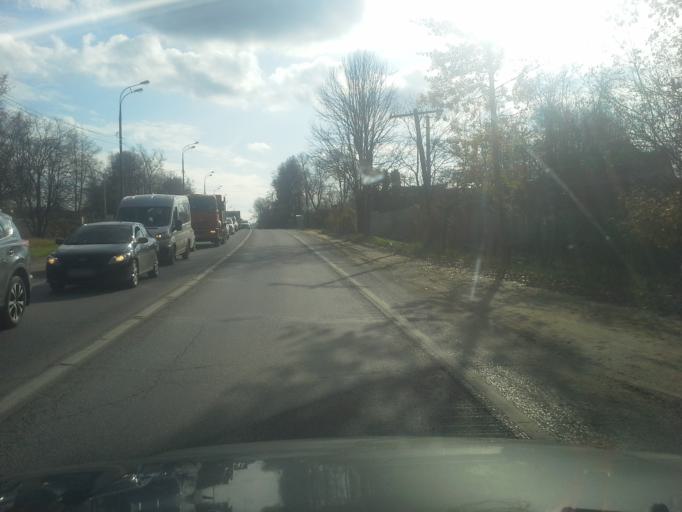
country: RU
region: Moskovskaya
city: Zvenigorod
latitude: 55.6984
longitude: 36.8848
